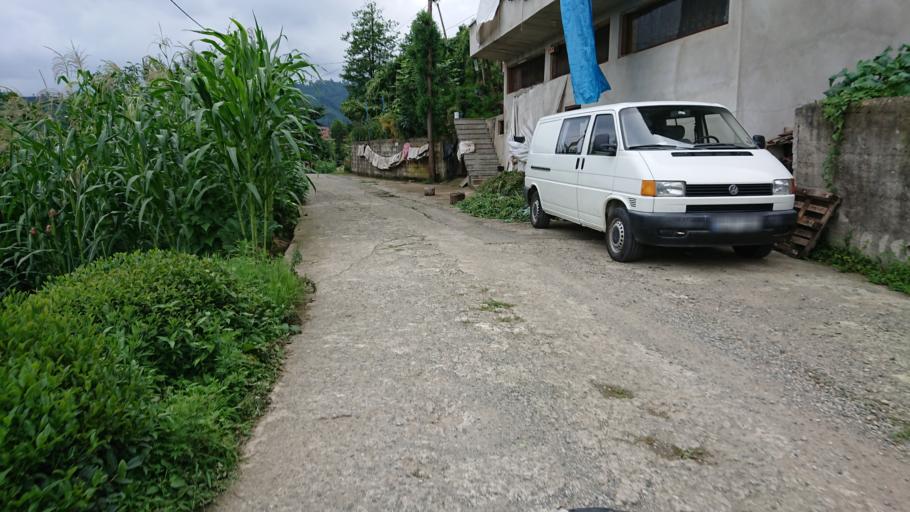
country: TR
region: Rize
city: Rize
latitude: 40.9701
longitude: 40.5153
